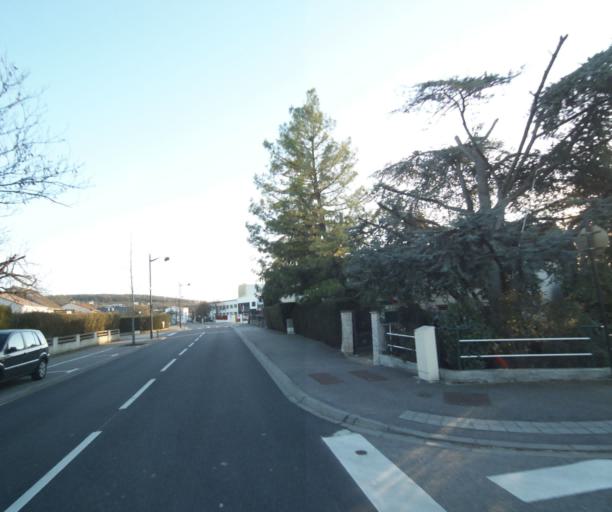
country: FR
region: Lorraine
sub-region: Departement de Meurthe-et-Moselle
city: Pulnoy
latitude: 48.7048
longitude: 6.2604
